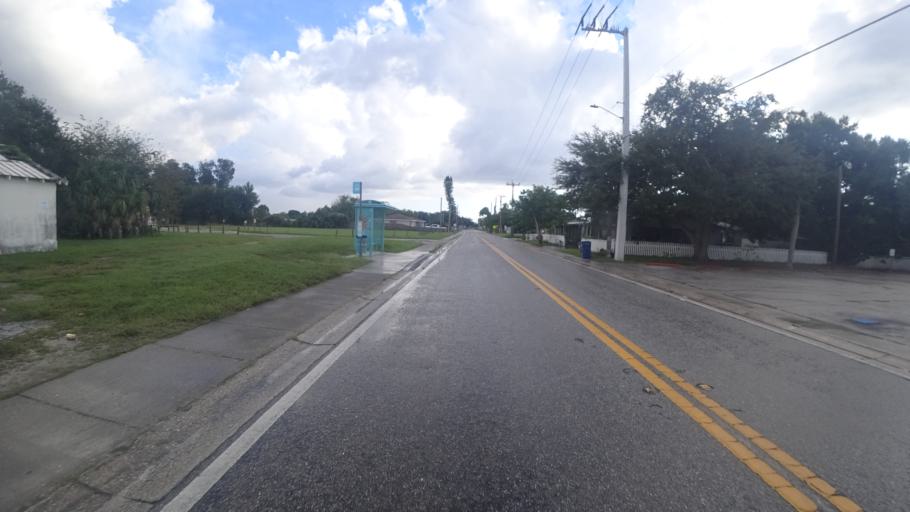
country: US
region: Florida
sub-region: Manatee County
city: Memphis
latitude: 27.5282
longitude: -82.5647
